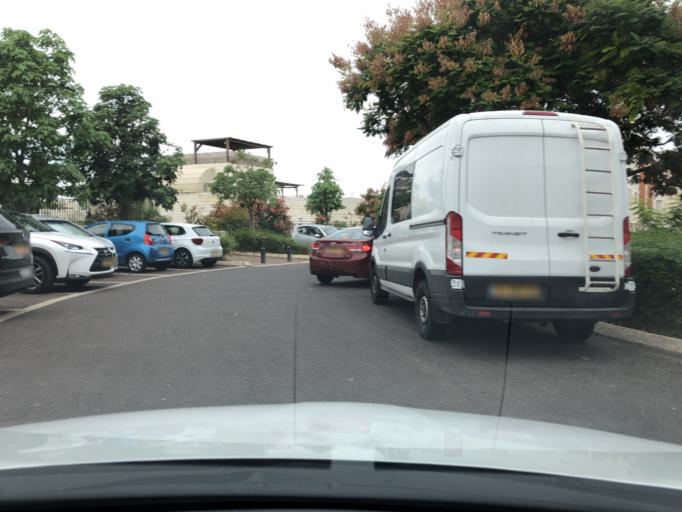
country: IL
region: Central District
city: Modiin
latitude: 31.9061
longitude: 35.0107
